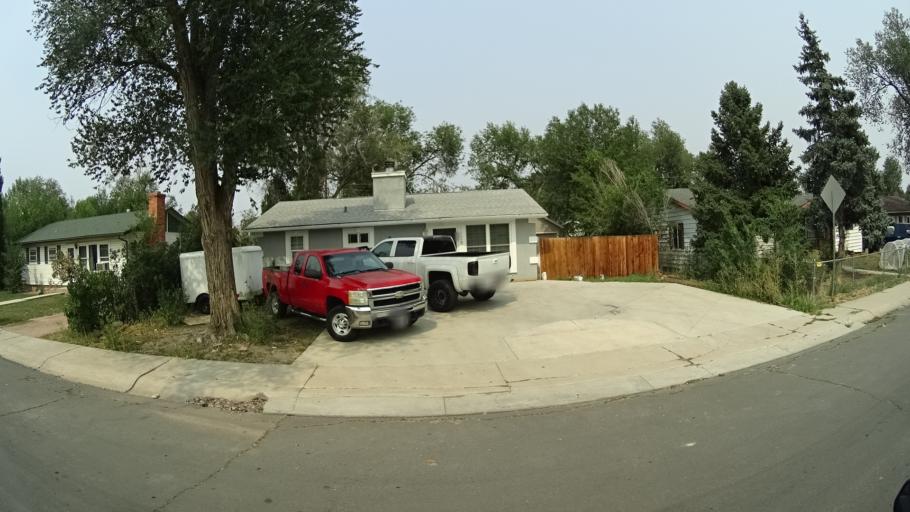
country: US
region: Colorado
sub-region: El Paso County
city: Colorado Springs
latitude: 38.7989
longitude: -104.8082
